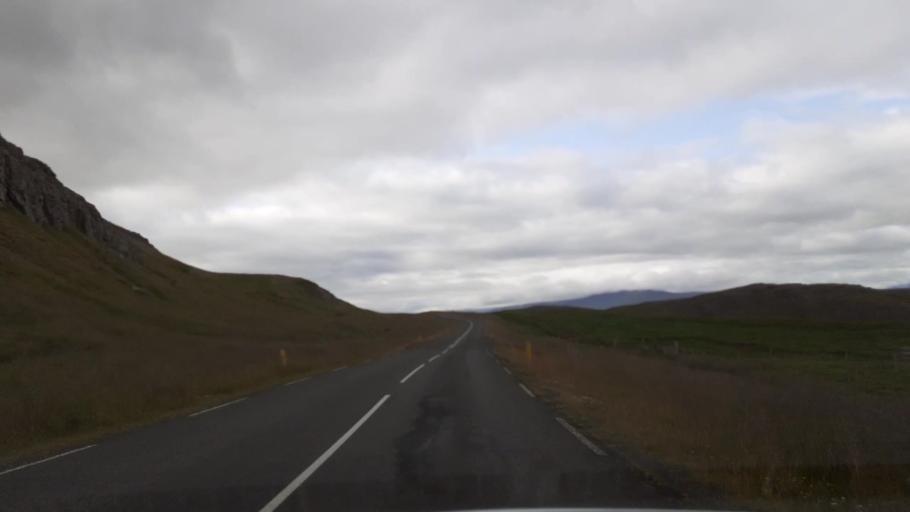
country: IS
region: Northeast
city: Akureyri
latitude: 65.8100
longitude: -18.0540
